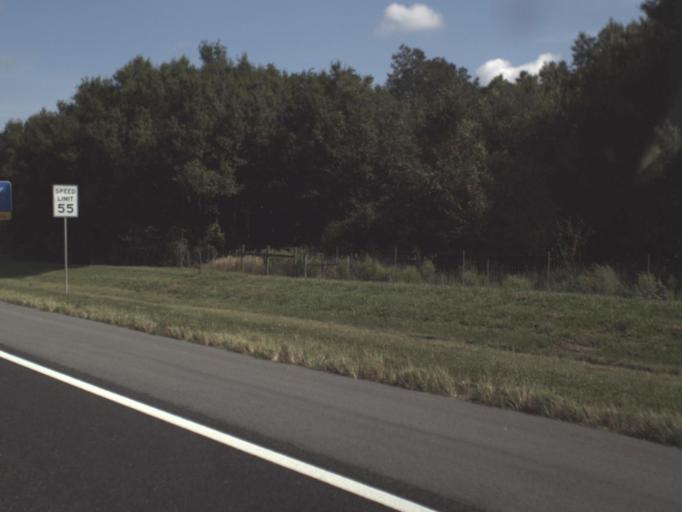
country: US
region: Florida
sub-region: Polk County
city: Fussels Corner
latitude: 28.0655
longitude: -81.8337
